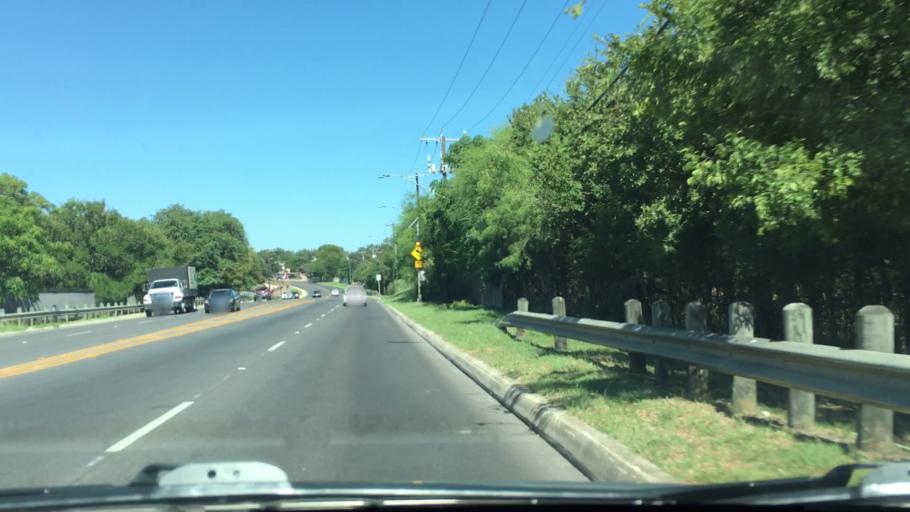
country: US
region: Texas
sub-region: Bexar County
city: Hollywood Park
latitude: 29.5794
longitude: -98.5010
